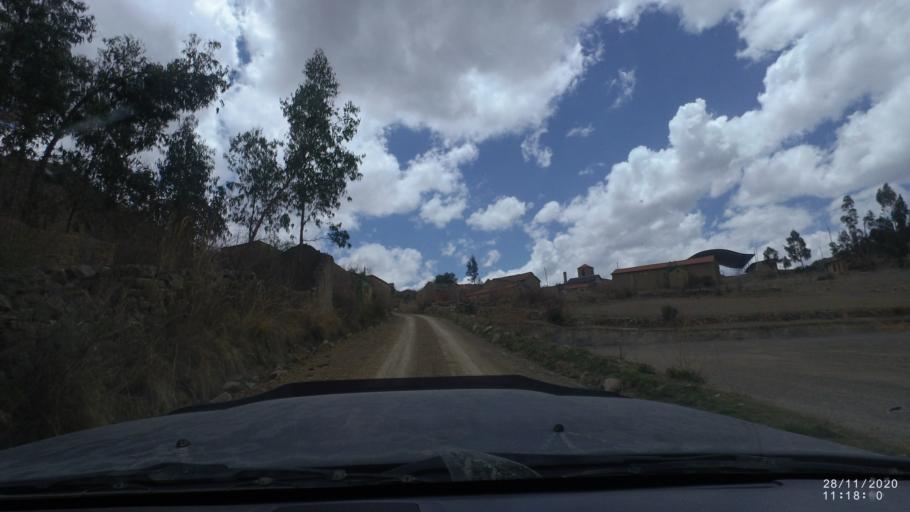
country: BO
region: Cochabamba
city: Tarata
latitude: -17.7532
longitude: -66.0752
